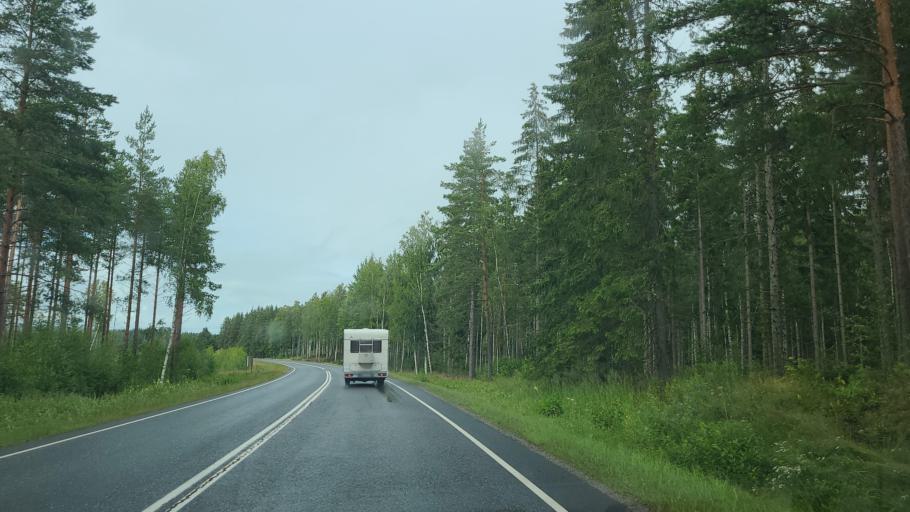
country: FI
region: Varsinais-Suomi
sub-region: Turku
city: Sauvo
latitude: 60.3245
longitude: 22.7131
